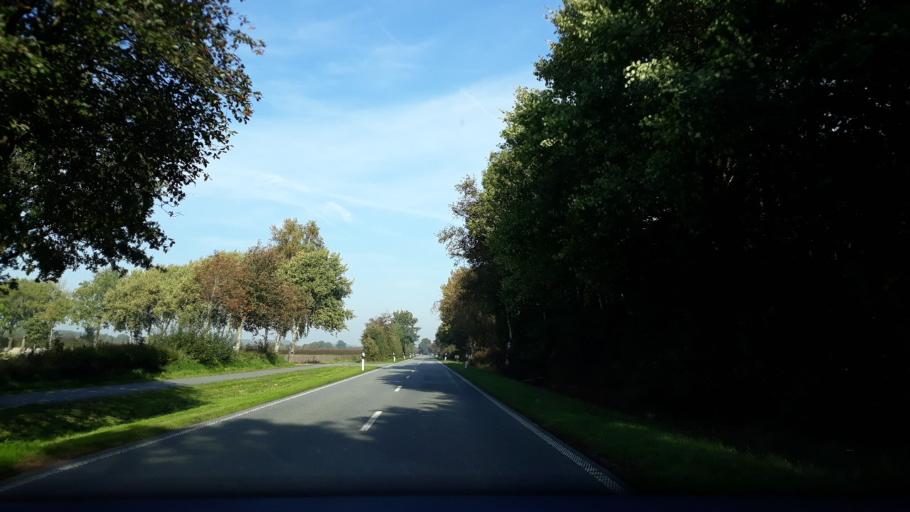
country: DE
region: Schleswig-Holstein
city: Klein Rheide
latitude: 54.4653
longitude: 9.4879
